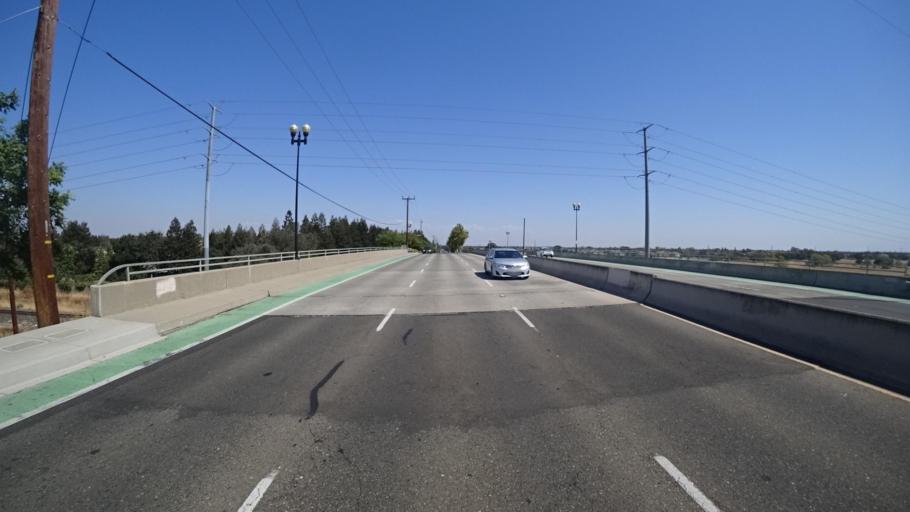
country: US
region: California
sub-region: Sacramento County
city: Laguna
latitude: 38.4084
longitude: -121.4547
